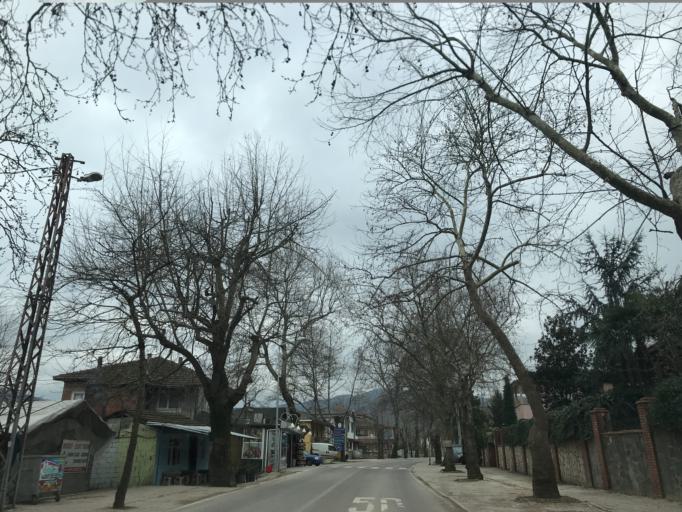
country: TR
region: Yalova
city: Kadikoy
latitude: 40.6196
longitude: 29.2186
